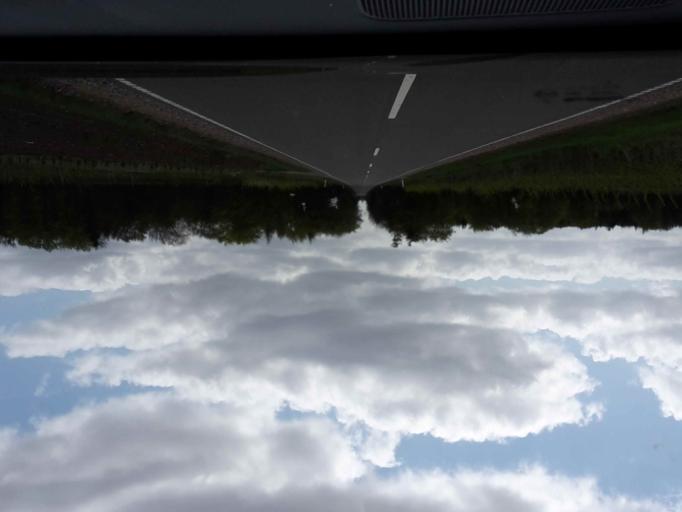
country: DK
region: South Denmark
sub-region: Varde Kommune
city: Olgod
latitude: 55.7009
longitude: 8.6066
